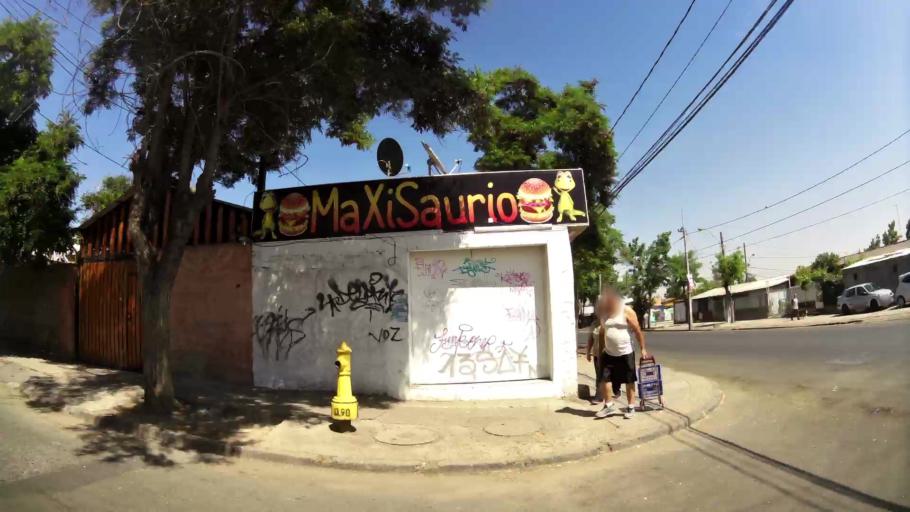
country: CL
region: Santiago Metropolitan
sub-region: Provincia de Santiago
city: La Pintana
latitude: -33.5607
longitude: -70.6683
